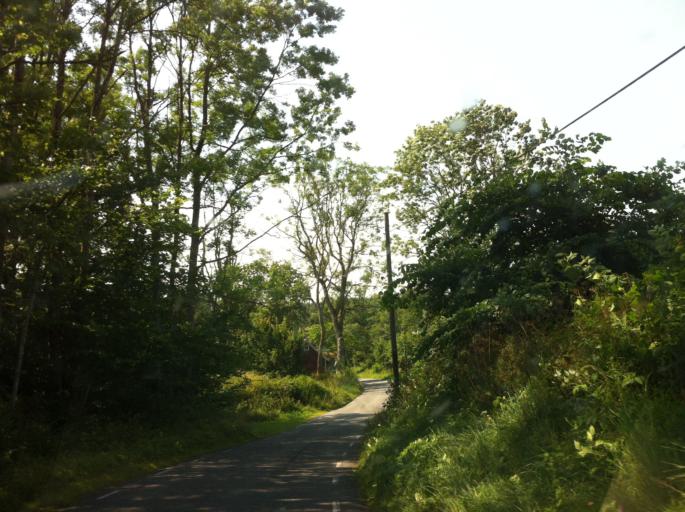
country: SE
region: Skane
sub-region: Hoors Kommun
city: Hoeoer
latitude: 56.0108
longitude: 13.5303
